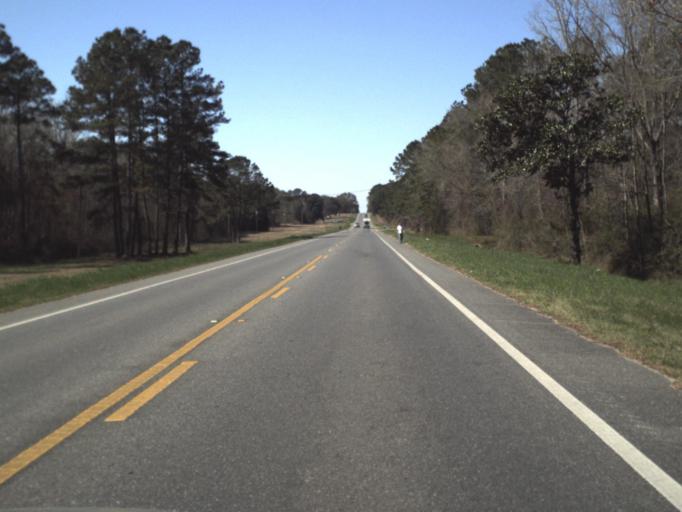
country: US
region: Florida
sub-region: Jackson County
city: Marianna
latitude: 30.7846
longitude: -85.2995
